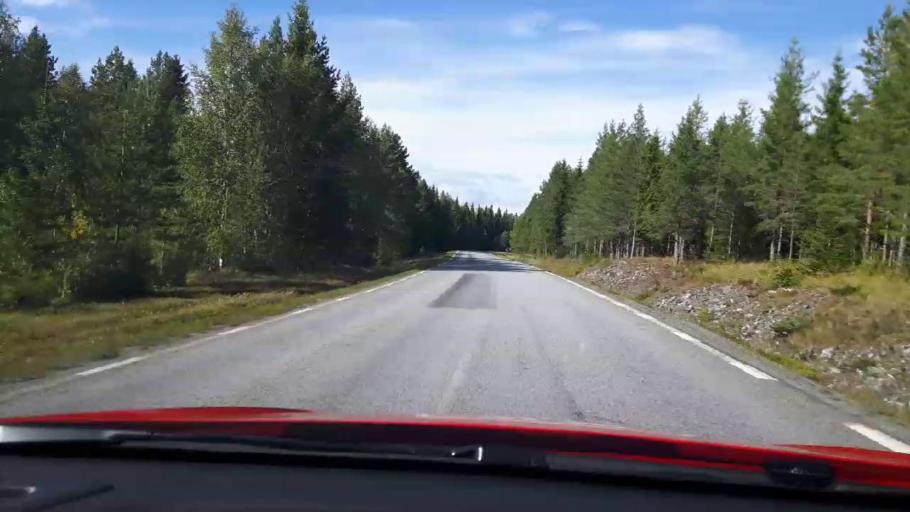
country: SE
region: Jaemtland
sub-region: OEstersunds Kommun
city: Ostersund
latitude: 63.0706
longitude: 14.4469
